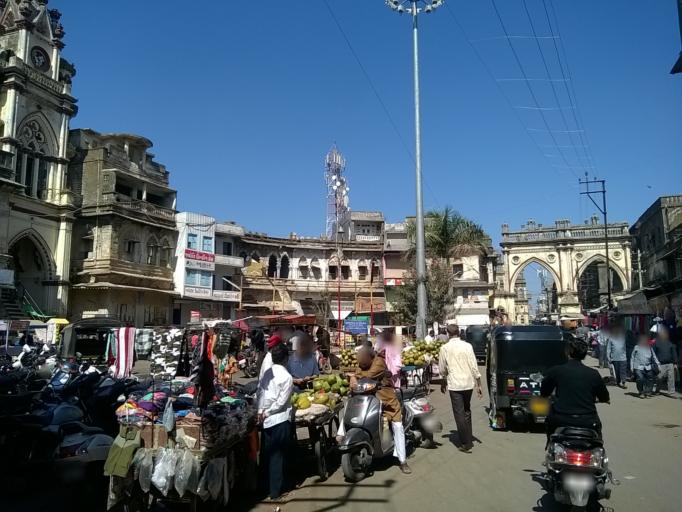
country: IN
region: Gujarat
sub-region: Junagadh
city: Junagadh
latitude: 21.5211
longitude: 70.4643
